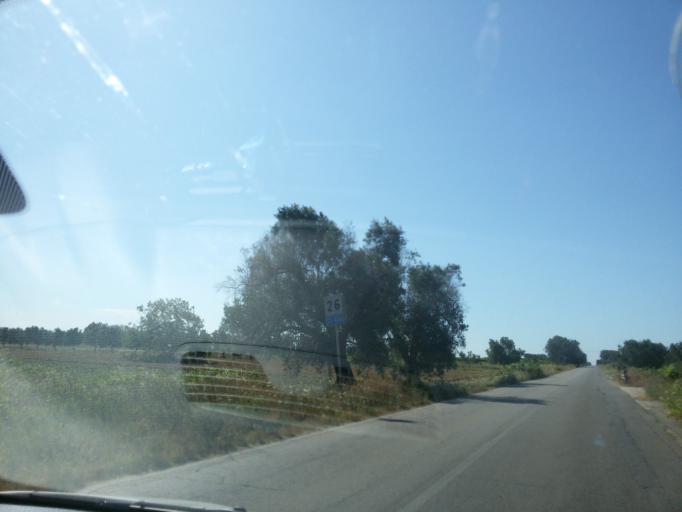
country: IT
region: Apulia
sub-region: Provincia di Brindisi
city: San Donaci
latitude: 40.4768
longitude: 17.8935
